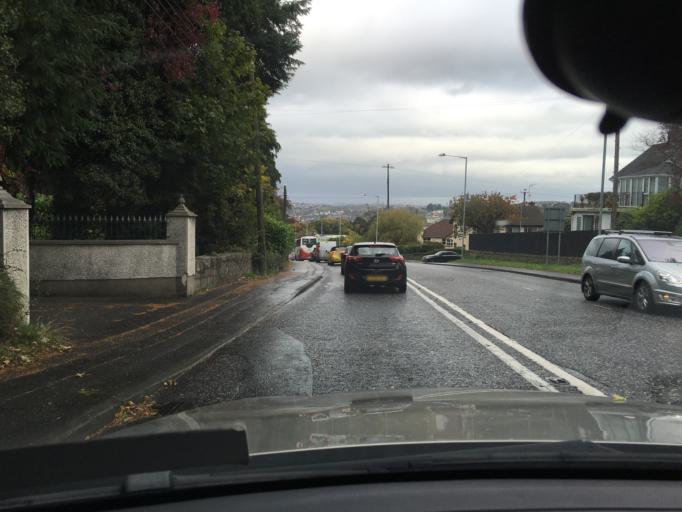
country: GB
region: Northern Ireland
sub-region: Newry and Mourne District
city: Newry
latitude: 54.1645
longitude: -6.3447
